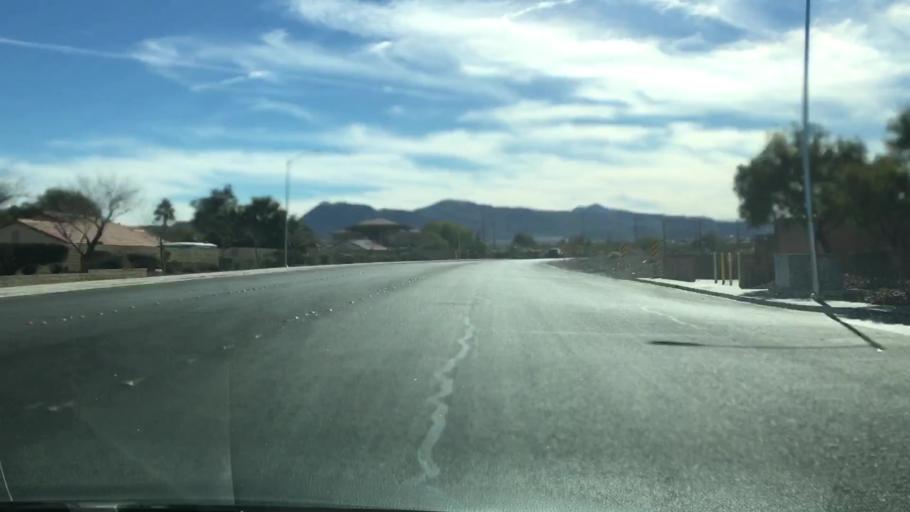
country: US
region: Nevada
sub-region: Clark County
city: Henderson
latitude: 36.0785
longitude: -115.0206
